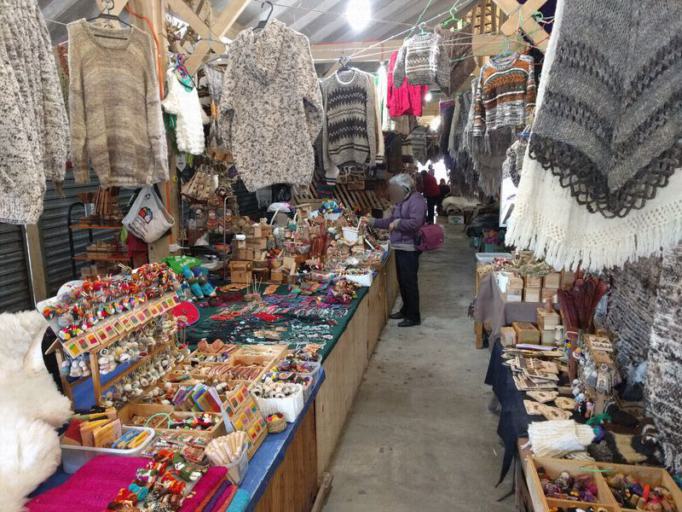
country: CL
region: Los Lagos
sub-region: Provincia de Chiloe
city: Castro
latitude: -42.3811
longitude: -73.6484
